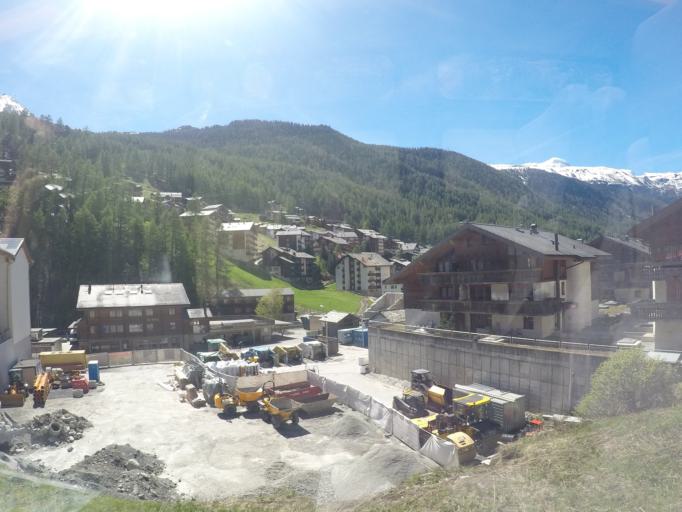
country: CH
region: Valais
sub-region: Visp District
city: Zermatt
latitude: 46.0285
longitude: 7.7525
